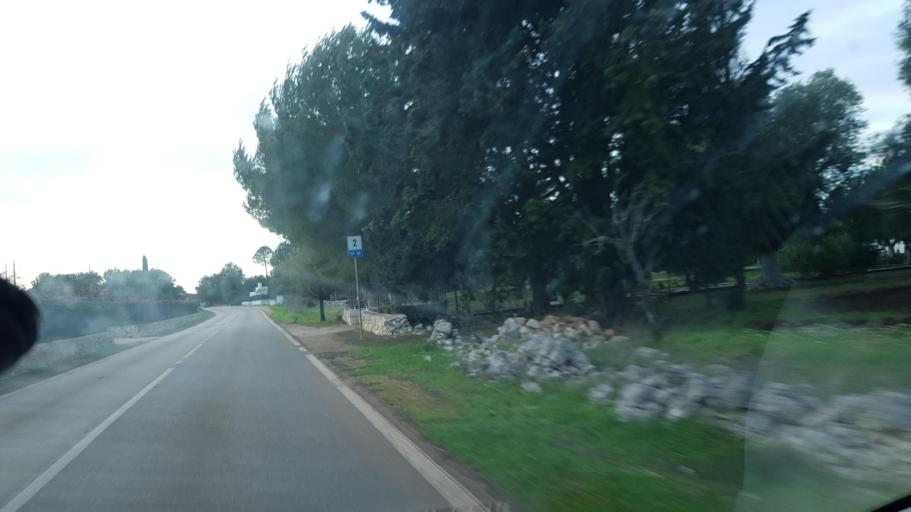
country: IT
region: Apulia
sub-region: Provincia di Brindisi
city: San Vito dei Normanni
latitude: 40.6479
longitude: 17.6716
